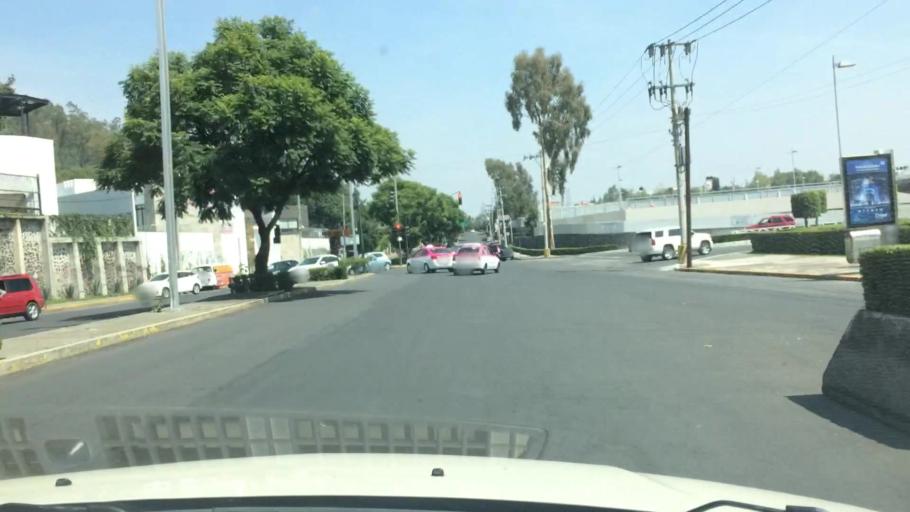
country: MX
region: Mexico City
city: Tlalpan
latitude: 19.3032
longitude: -99.1930
